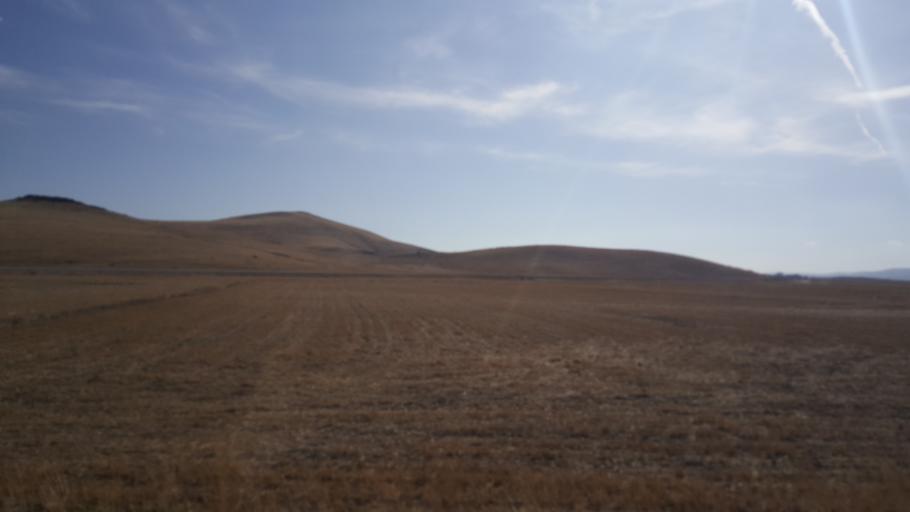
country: TR
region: Ankara
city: Yenice
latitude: 39.3830
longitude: 32.8201
